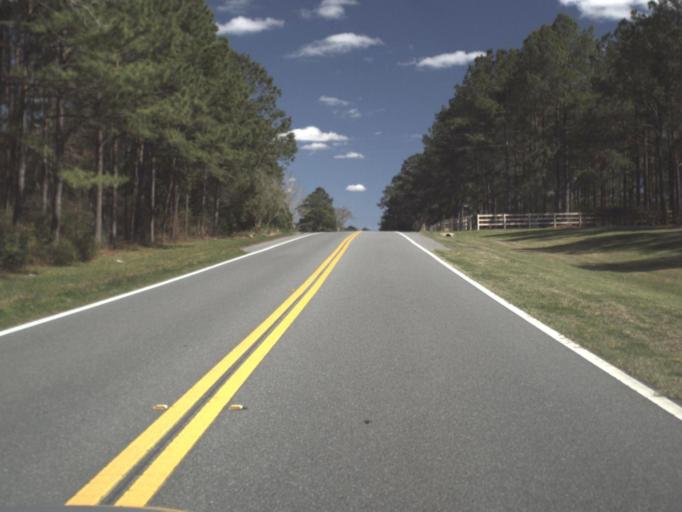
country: US
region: Florida
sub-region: Gadsden County
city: Chattahoochee
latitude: 30.7027
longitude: -84.7893
